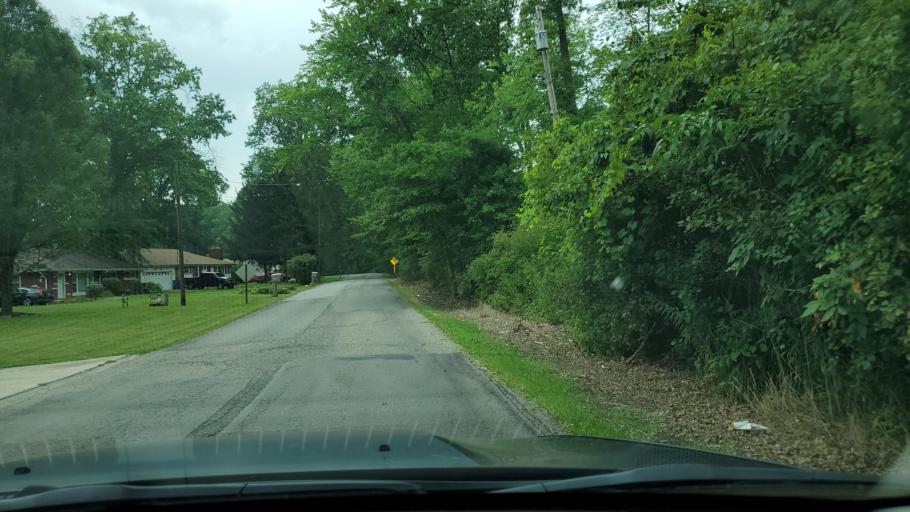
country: US
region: Ohio
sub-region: Trumbull County
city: Bolindale
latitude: 41.2252
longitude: -80.7732
